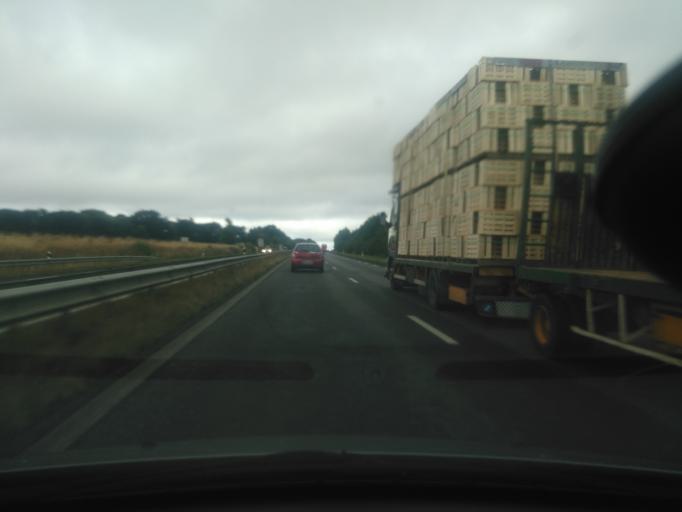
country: FR
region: Brittany
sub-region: Departement d'Ille-et-Vilaine
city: Vignoc
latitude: 48.2607
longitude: -1.7774
